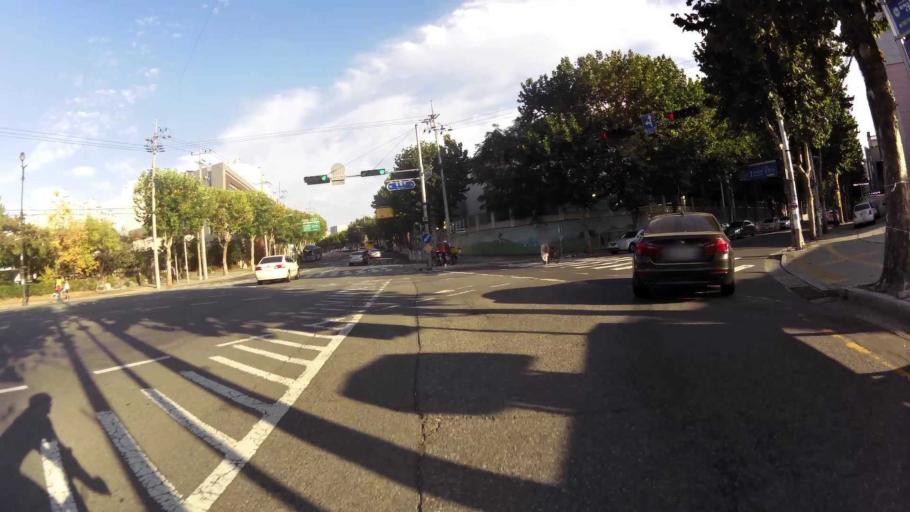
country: KR
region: Daegu
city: Daegu
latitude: 35.8661
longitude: 128.6388
